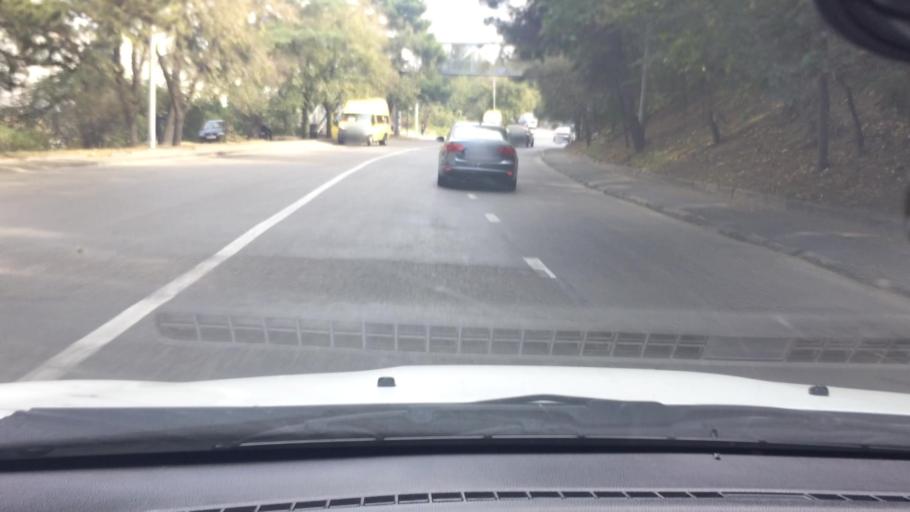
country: GE
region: T'bilisi
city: Tbilisi
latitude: 41.6708
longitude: 44.8451
